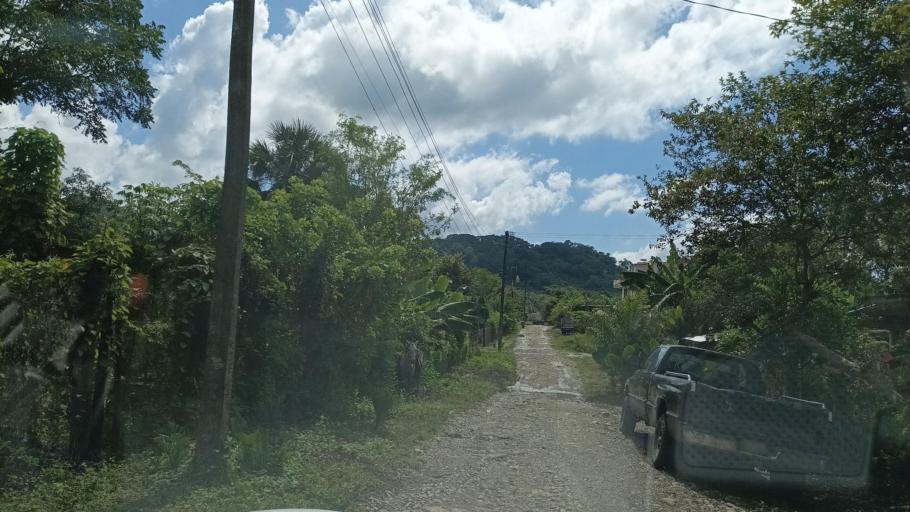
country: MX
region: Veracruz
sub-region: Tantoyuca
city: El Lindero
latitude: 21.1959
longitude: -98.1441
